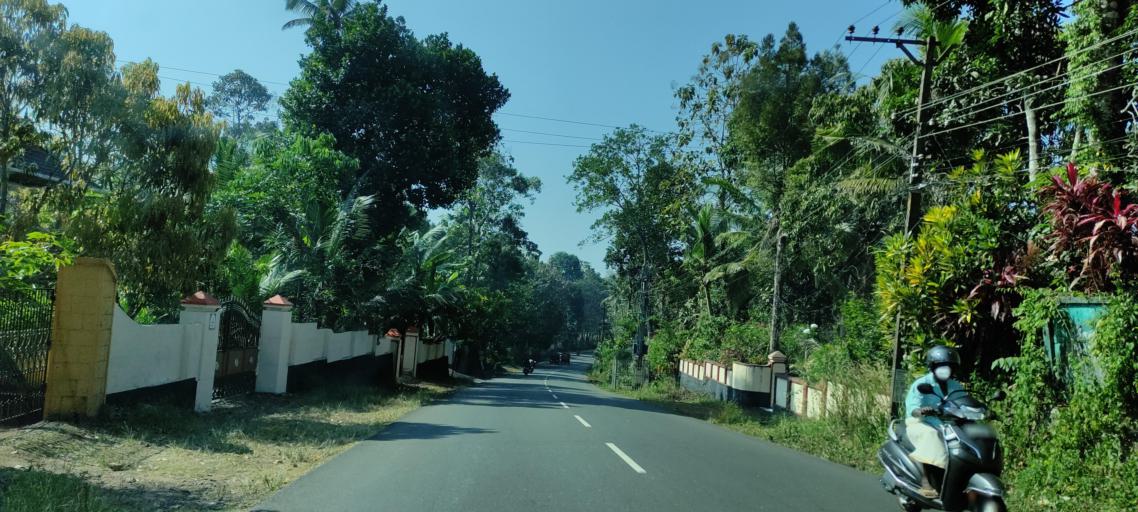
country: IN
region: Kerala
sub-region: Pattanamtitta
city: Adur
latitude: 9.1184
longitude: 76.7004
